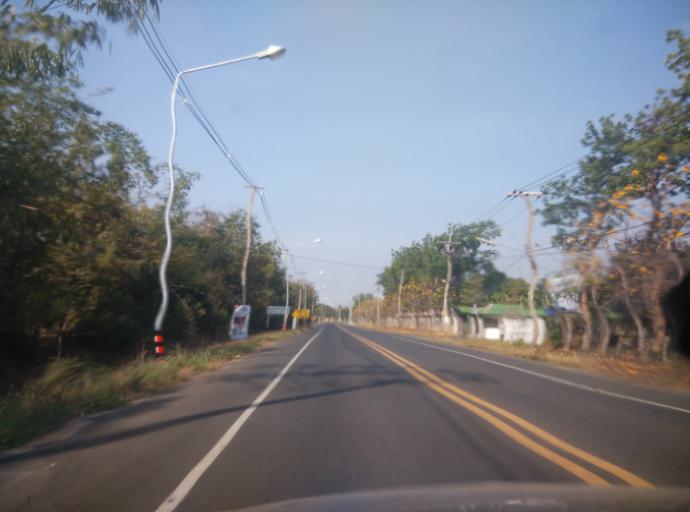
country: TH
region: Sisaket
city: Si Sa Ket
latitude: 15.1122
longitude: 104.2727
